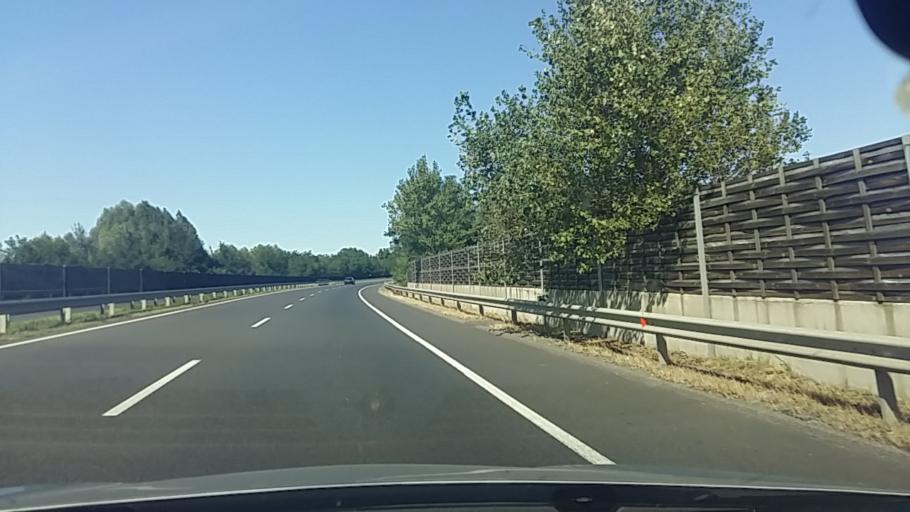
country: HU
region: Szabolcs-Szatmar-Bereg
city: Nyiregyhaza
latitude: 47.8918
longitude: 21.7100
